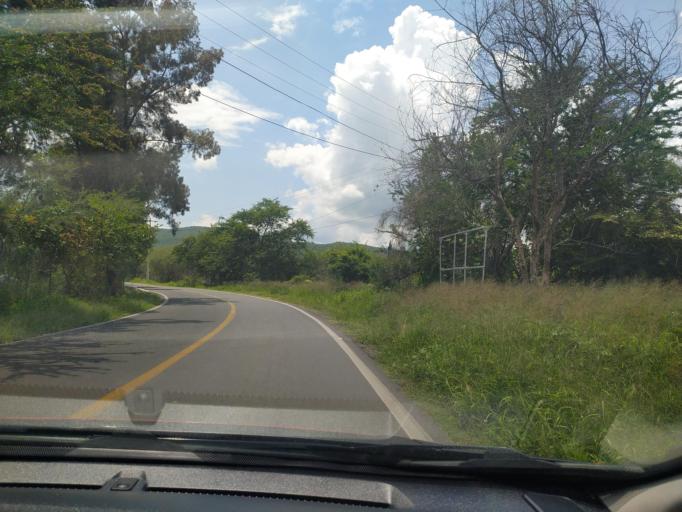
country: MX
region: Jalisco
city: Villa Corona
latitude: 20.4126
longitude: -103.6728
